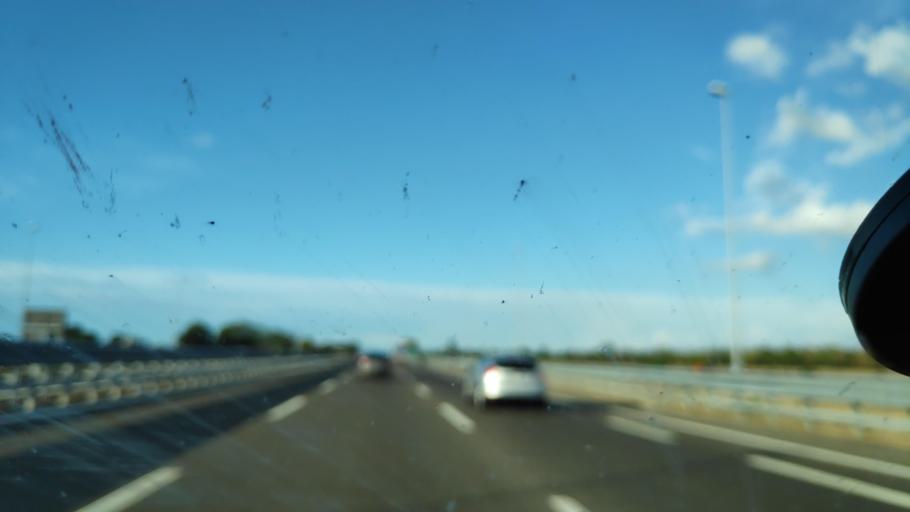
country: IT
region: Piedmont
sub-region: Provincia di Alessandria
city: Tortona
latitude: 44.9369
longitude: 8.8547
